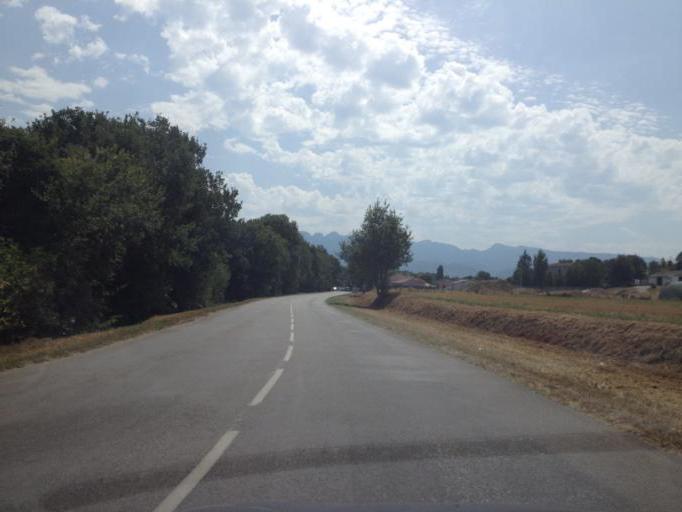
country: FR
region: Rhone-Alpes
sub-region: Departement de la Drome
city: Chatuzange-le-Goubet
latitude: 45.0131
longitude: 5.0843
